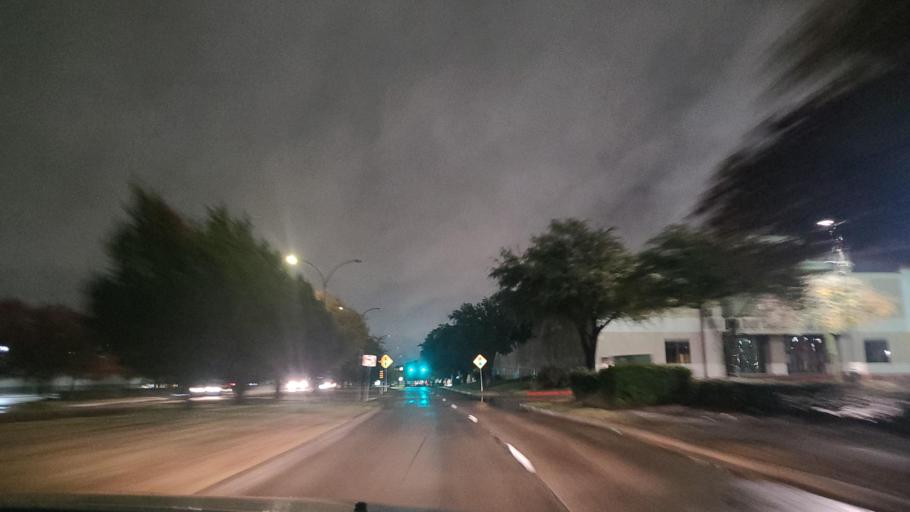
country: US
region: Texas
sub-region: Tarrant County
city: Dalworthington Gardens
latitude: 32.6819
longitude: -97.1257
